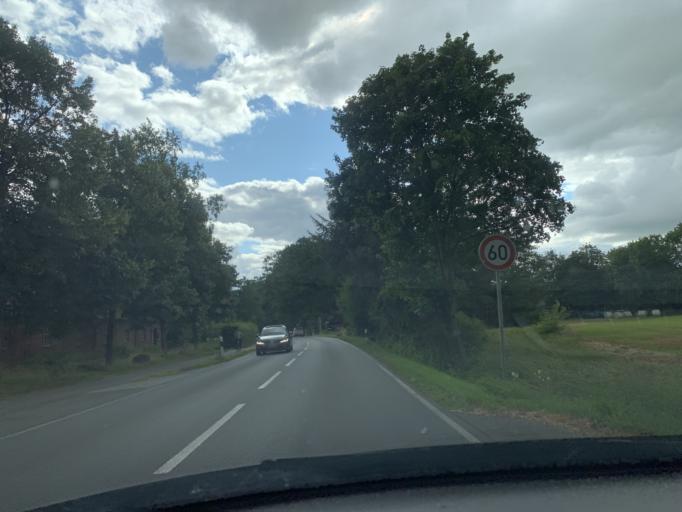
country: DE
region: Lower Saxony
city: Westerstede
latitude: 53.2255
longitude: 7.9004
